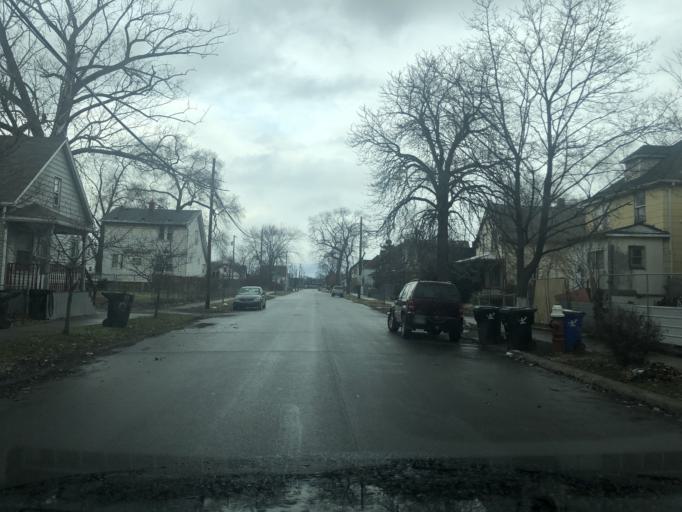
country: US
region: Michigan
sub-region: Wayne County
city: River Rouge
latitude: 42.3072
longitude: -83.1134
